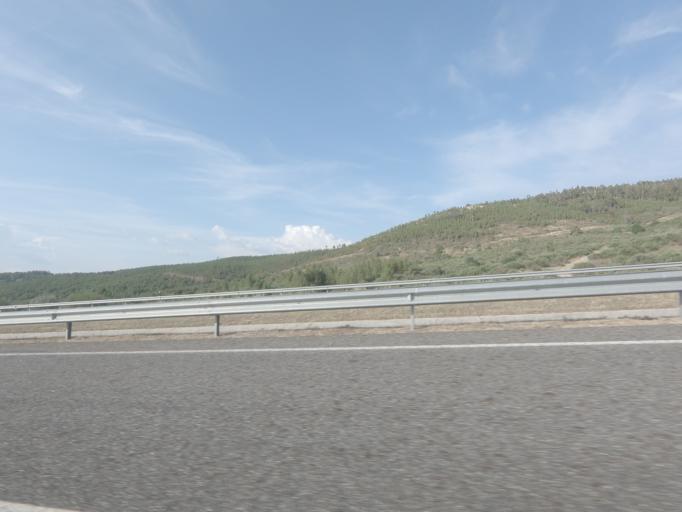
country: ES
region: Galicia
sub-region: Provincia de Ourense
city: Oimbra
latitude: 41.8634
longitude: -7.4281
